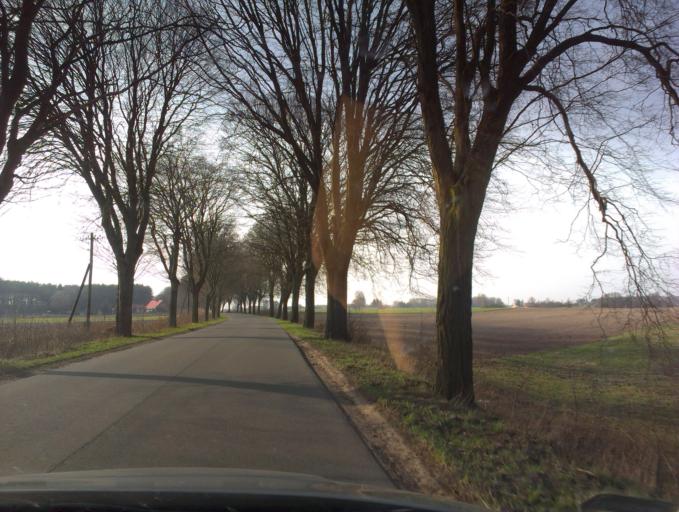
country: PL
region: Greater Poland Voivodeship
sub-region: Powiat zlotowski
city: Lipka
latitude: 53.4639
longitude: 17.3162
